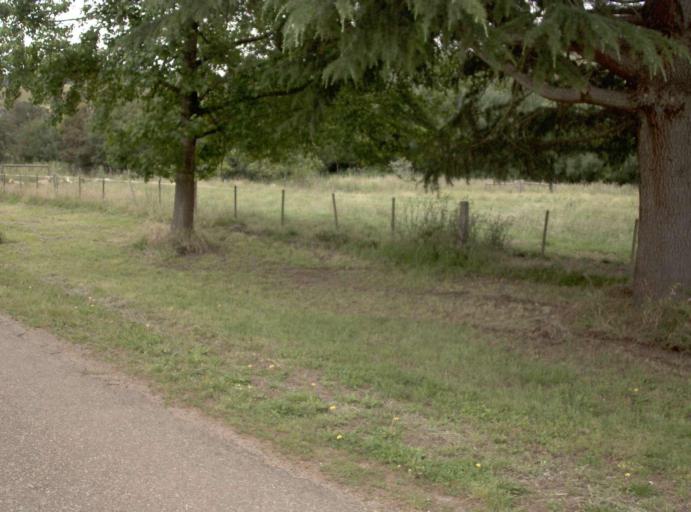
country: AU
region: Victoria
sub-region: East Gippsland
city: Bairnsdale
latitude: -37.4564
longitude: 147.2511
